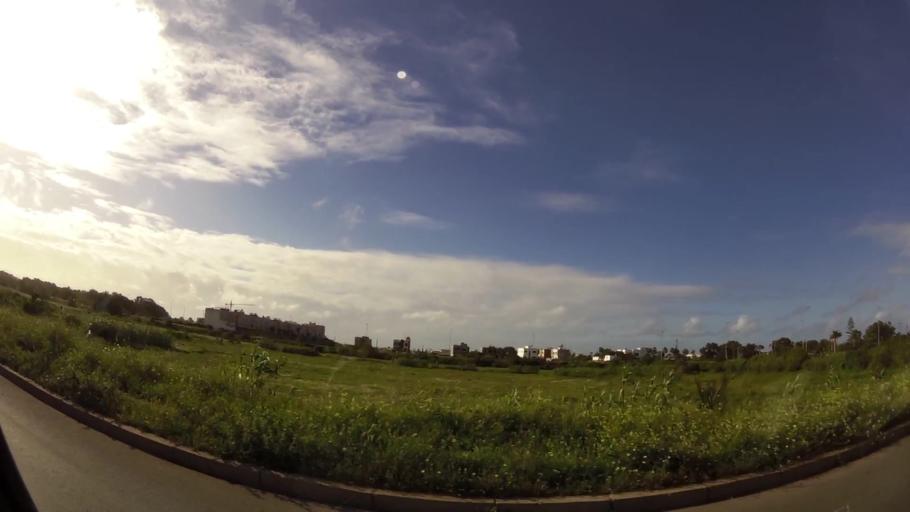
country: MA
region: Grand Casablanca
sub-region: Mohammedia
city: Mohammedia
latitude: 33.7049
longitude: -7.3742
